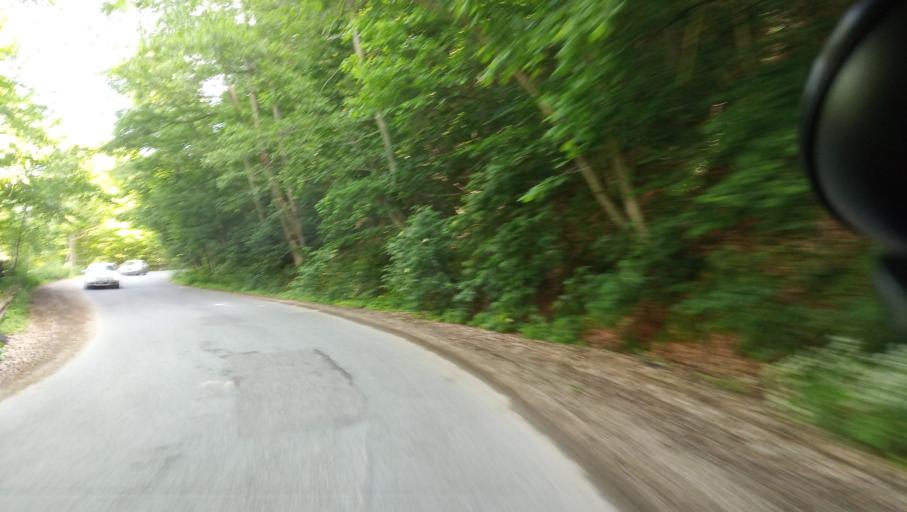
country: RO
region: Cluj
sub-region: Comuna Capusu Mare
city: Capusu Mare
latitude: 46.7131
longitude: 23.2754
